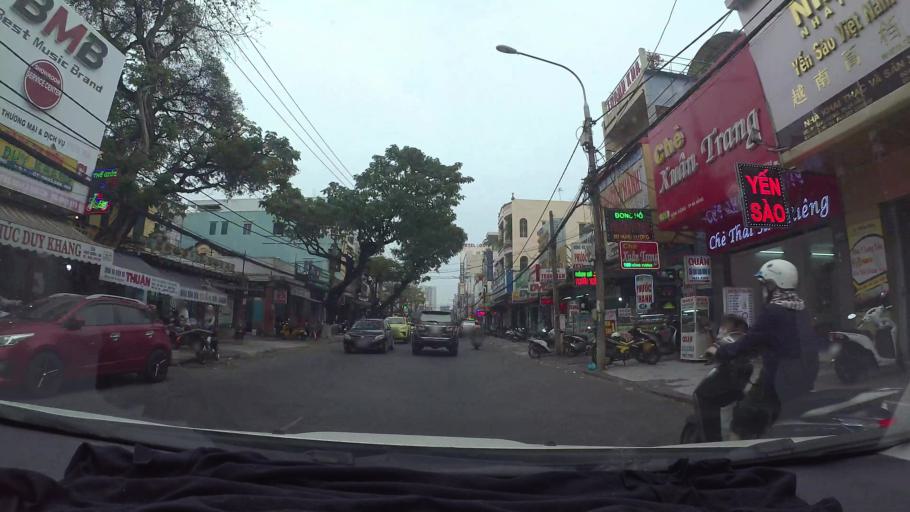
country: VN
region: Da Nang
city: Da Nang
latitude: 16.0676
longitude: 108.2160
